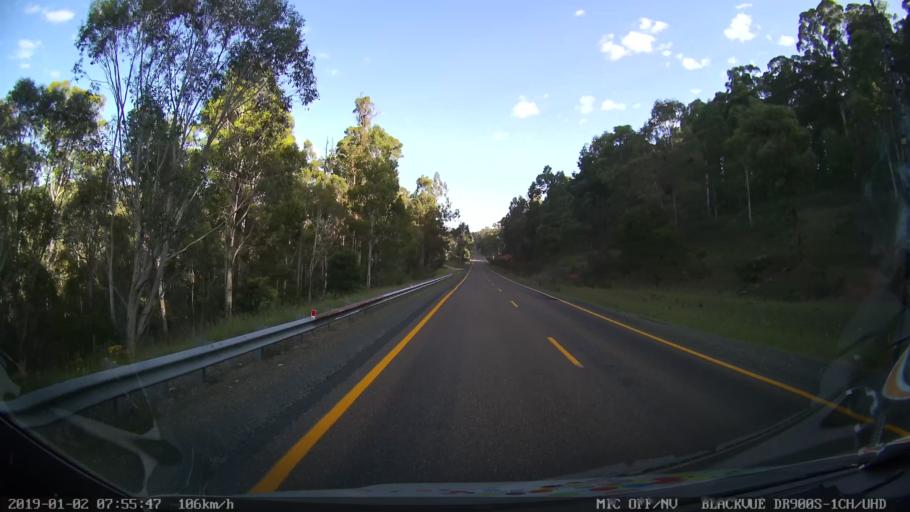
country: AU
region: New South Wales
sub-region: Tumut Shire
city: Tumut
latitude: -35.6795
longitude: 148.4864
